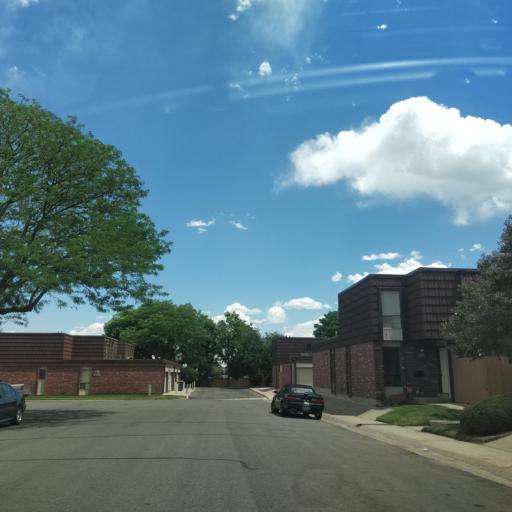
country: US
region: Colorado
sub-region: Jefferson County
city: Lakewood
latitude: 39.6826
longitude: -105.1022
